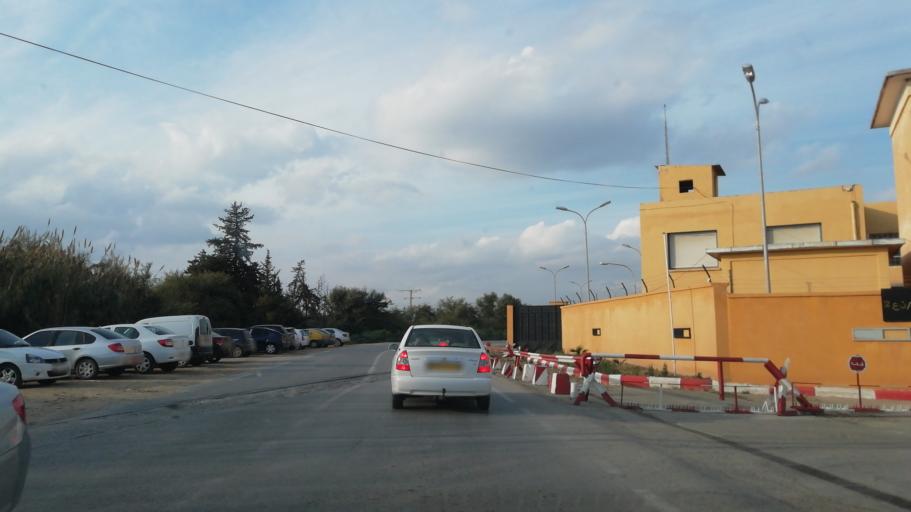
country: DZ
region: Mascara
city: Mascara
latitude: 35.5992
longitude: 0.0533
